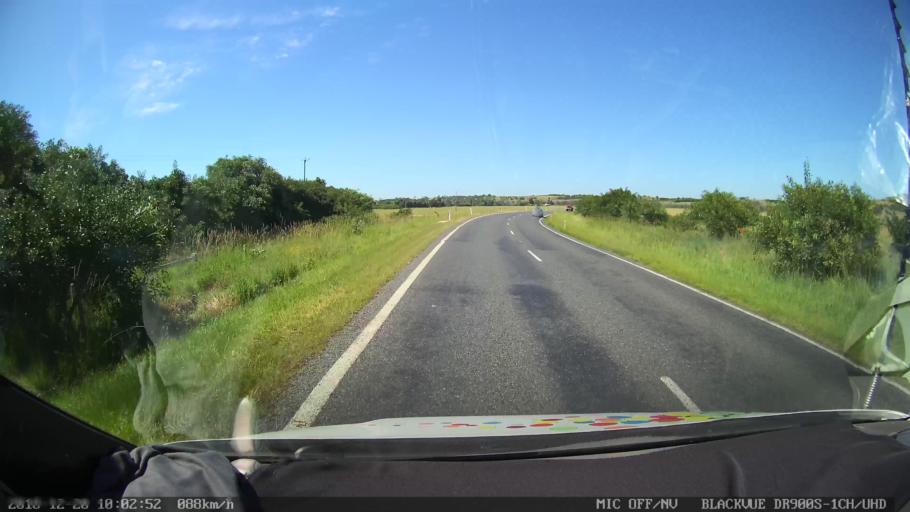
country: AU
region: New South Wales
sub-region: Lismore Municipality
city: East Lismore
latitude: -28.8633
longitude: 153.2604
